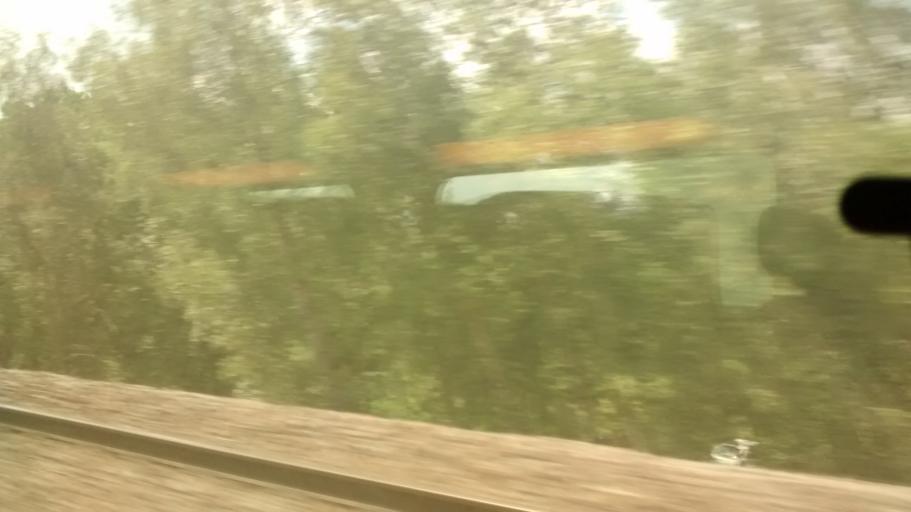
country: FR
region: Bourgogne
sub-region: Departement de Saone-et-Loire
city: Saint-Leu
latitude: 46.7547
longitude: 4.5027
